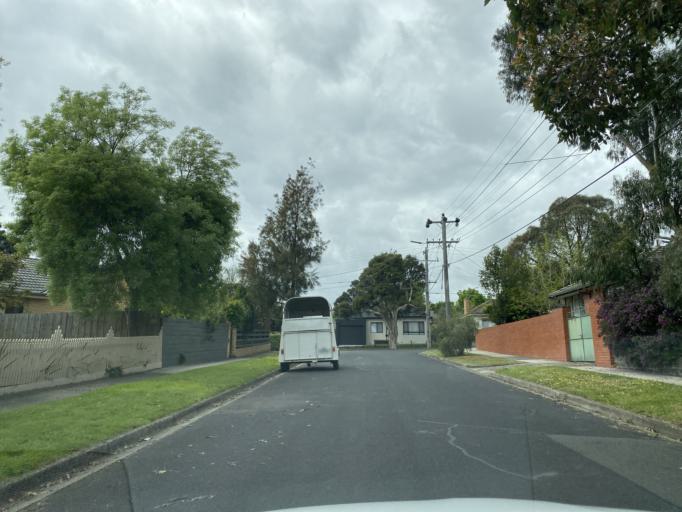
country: AU
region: Victoria
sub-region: Whitehorse
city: Burwood
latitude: -37.8435
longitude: 145.1287
